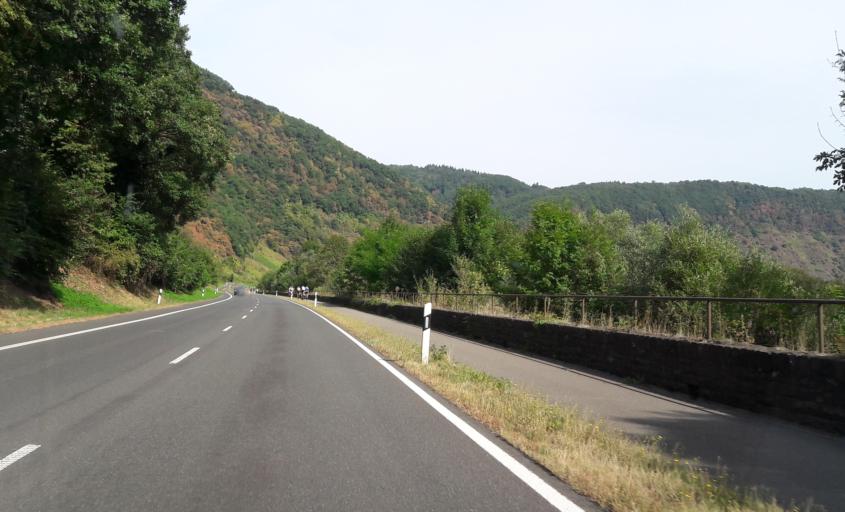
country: DE
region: Rheinland-Pfalz
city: Mesenich
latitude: 50.0991
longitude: 7.1914
